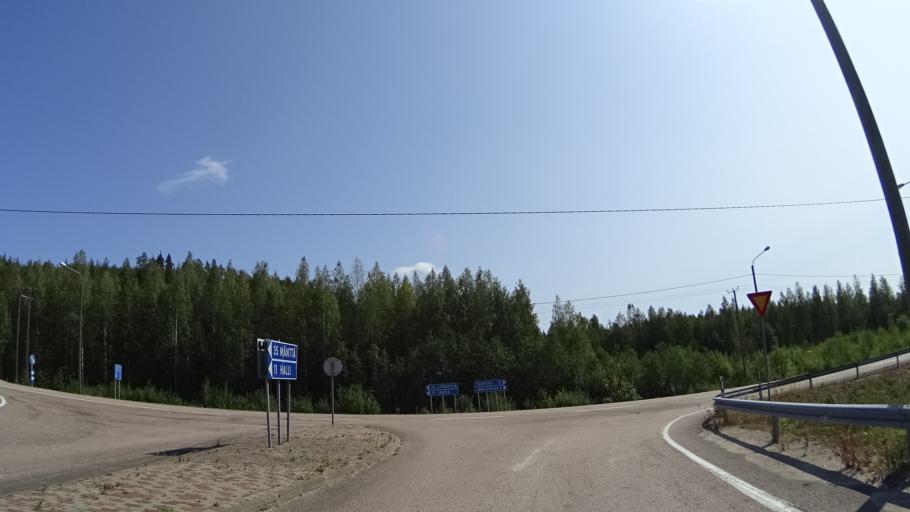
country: FI
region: Central Finland
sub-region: Jaemsae
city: Jaemsae
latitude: 61.7771
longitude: 24.8926
